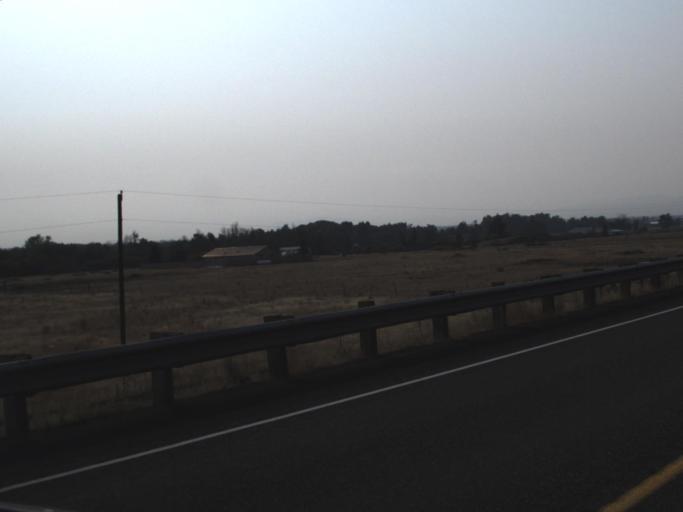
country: US
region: Washington
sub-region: Kittitas County
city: Ellensburg
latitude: 47.0631
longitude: -120.6221
